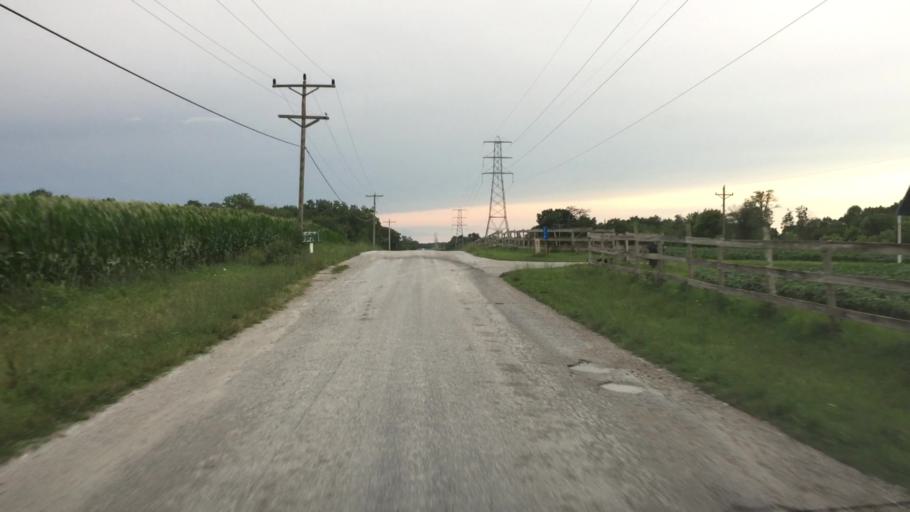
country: US
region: Illinois
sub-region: Hancock County
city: Hamilton
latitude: 40.3716
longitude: -91.3613
